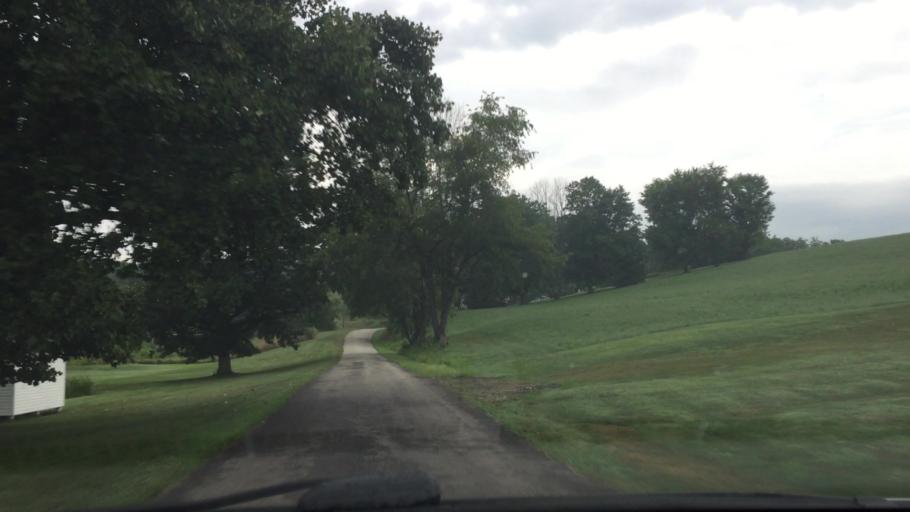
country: US
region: Pennsylvania
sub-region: Washington County
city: McMurray
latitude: 40.1765
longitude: -80.1009
